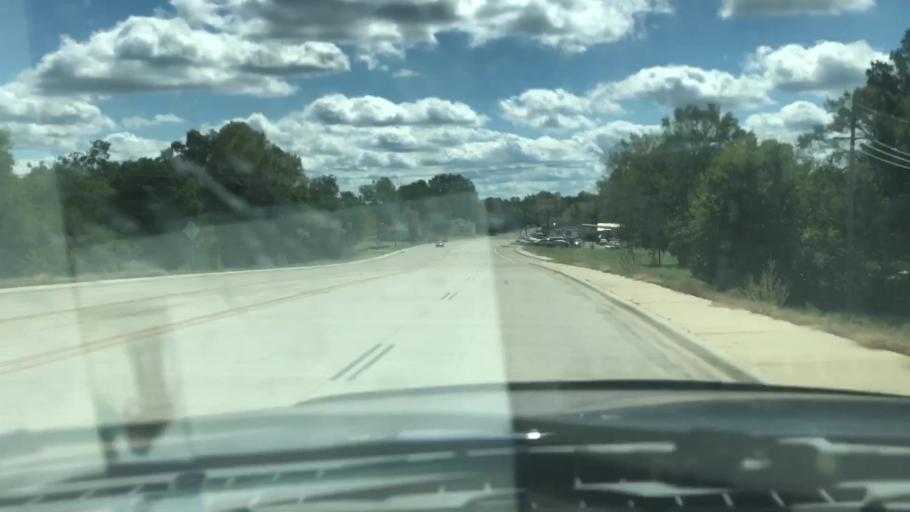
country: US
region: Texas
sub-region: Bowie County
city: Texarkana
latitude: 33.4126
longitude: -94.0610
